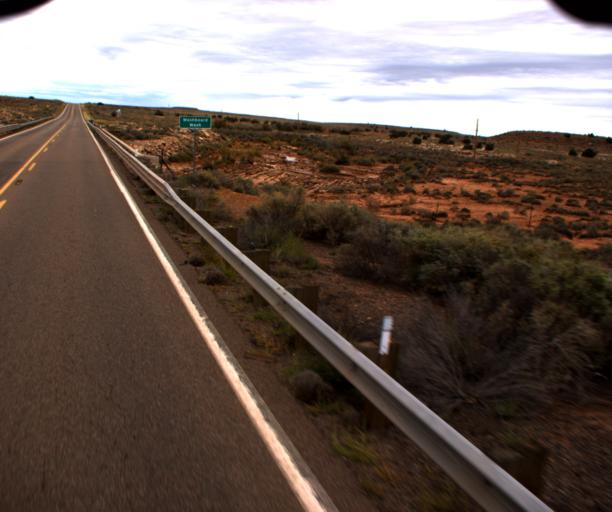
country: US
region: Arizona
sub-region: Navajo County
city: Holbrook
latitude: 34.7723
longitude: -110.1279
